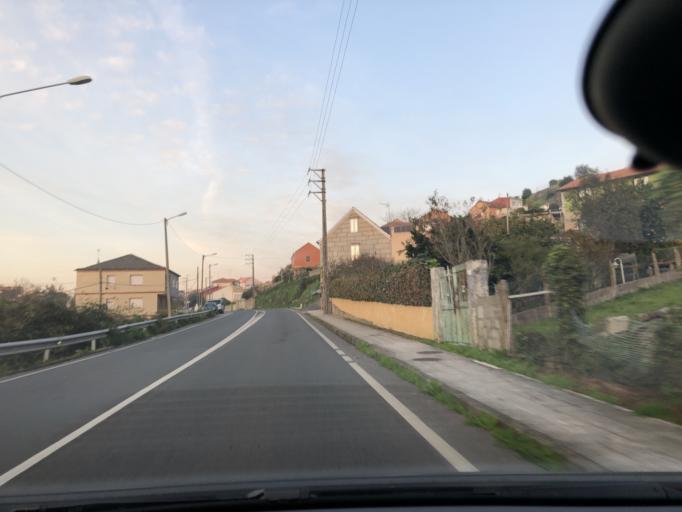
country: ES
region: Galicia
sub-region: Provincia de Pontevedra
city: Marin
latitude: 42.3830
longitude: -8.7147
